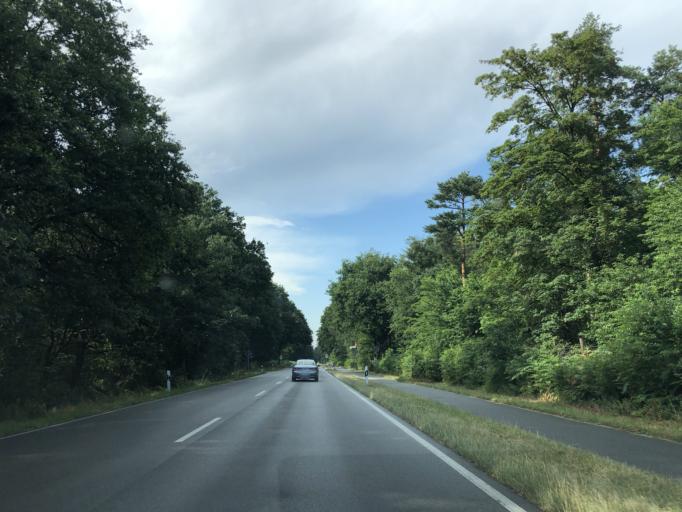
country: DE
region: North Rhine-Westphalia
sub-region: Regierungsbezirk Dusseldorf
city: Kranenburg
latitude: 51.7304
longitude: 6.0365
